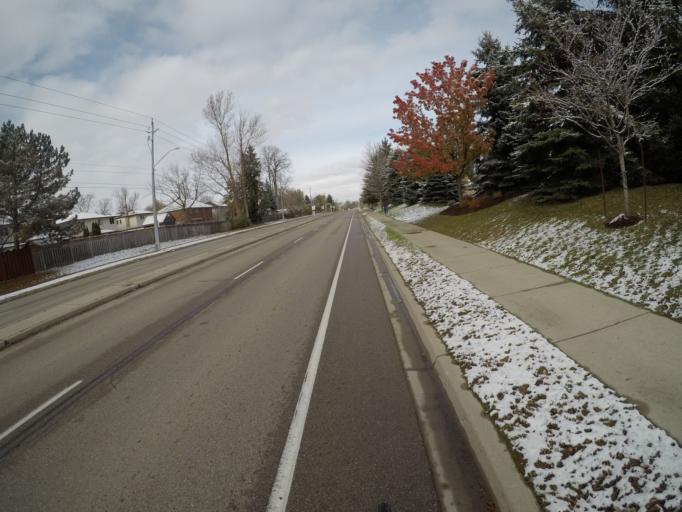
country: CA
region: Ontario
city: Waterloo
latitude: 43.5010
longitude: -80.4940
